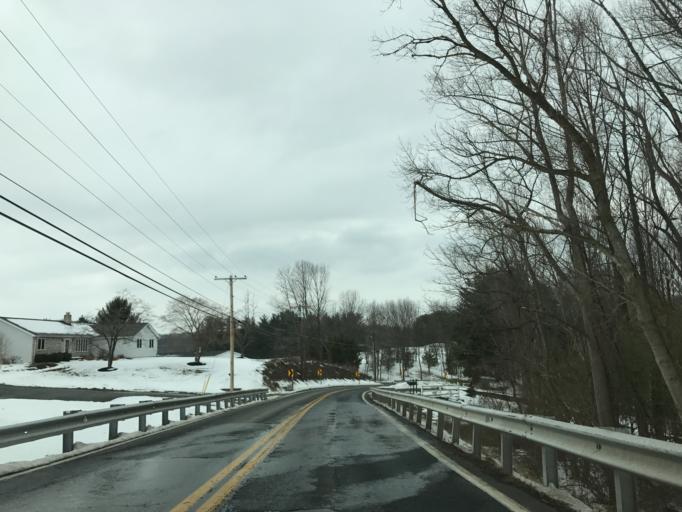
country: US
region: Maryland
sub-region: Harford County
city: Bel Air North
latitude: 39.6038
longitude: -76.3971
